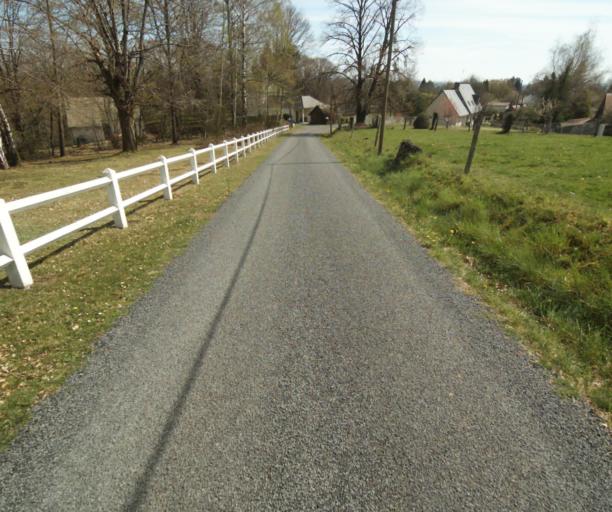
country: FR
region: Limousin
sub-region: Departement de la Correze
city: Seilhac
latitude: 45.3929
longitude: 1.7691
